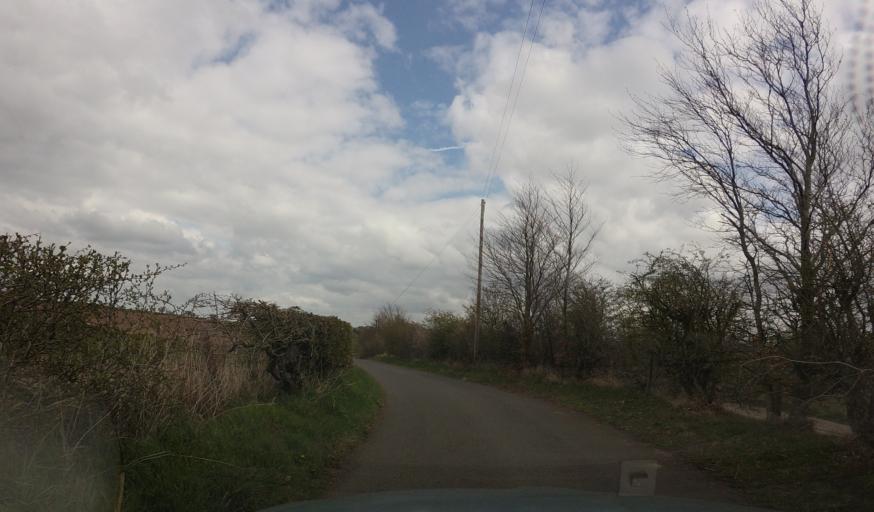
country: GB
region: Scotland
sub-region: Midlothian
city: Gorebridge
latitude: 55.8350
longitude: -3.0164
